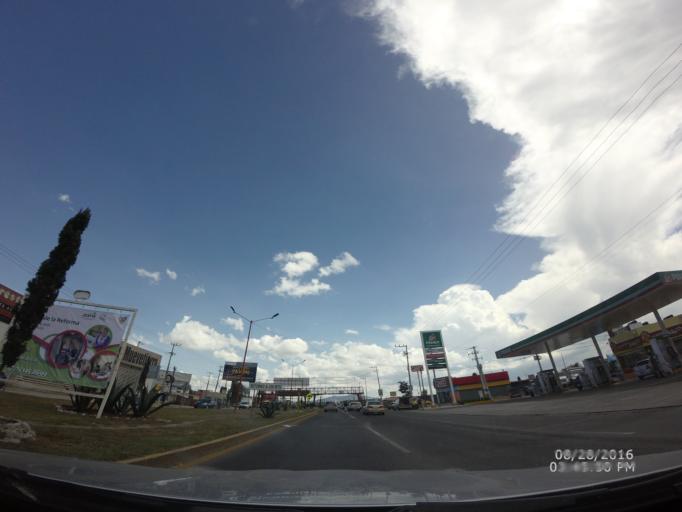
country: MX
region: Hidalgo
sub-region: Mineral de la Reforma
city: PRI Chacon
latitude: 20.0800
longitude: -98.7453
